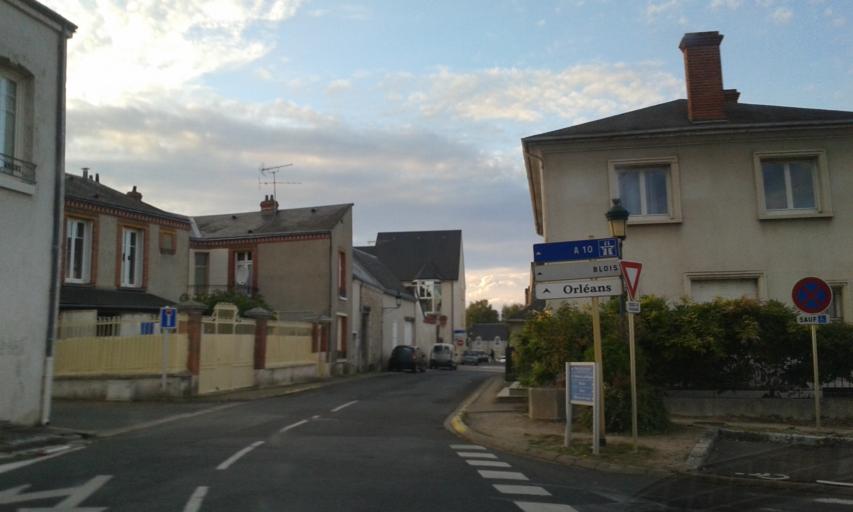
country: FR
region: Centre
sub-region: Departement du Loiret
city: Meung-sur-Loire
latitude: 47.8260
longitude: 1.6930
